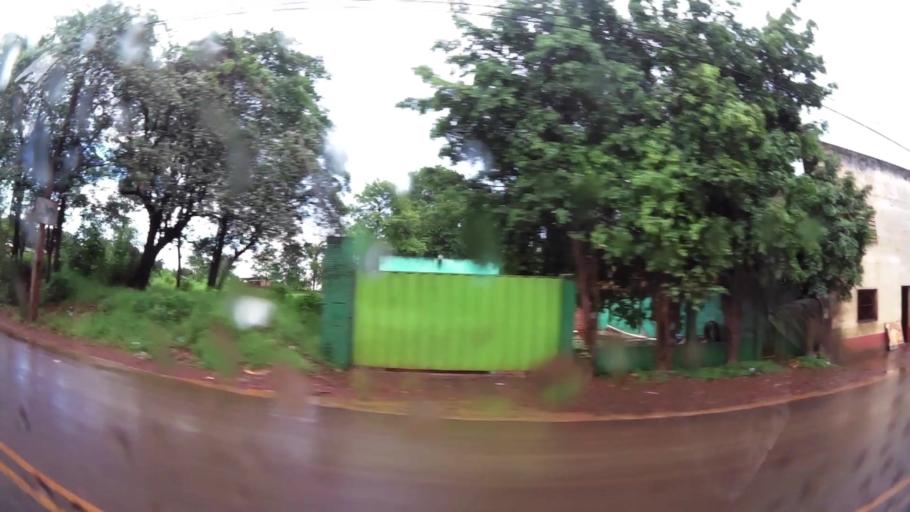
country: PY
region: Alto Parana
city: Presidente Franco
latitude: -25.5558
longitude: -54.6527
